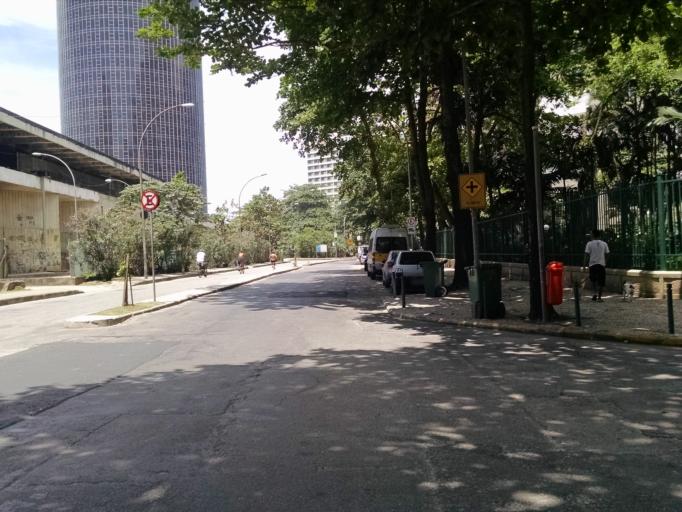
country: BR
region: Rio de Janeiro
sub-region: Rio De Janeiro
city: Rio de Janeiro
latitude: -22.9962
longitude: -43.2563
